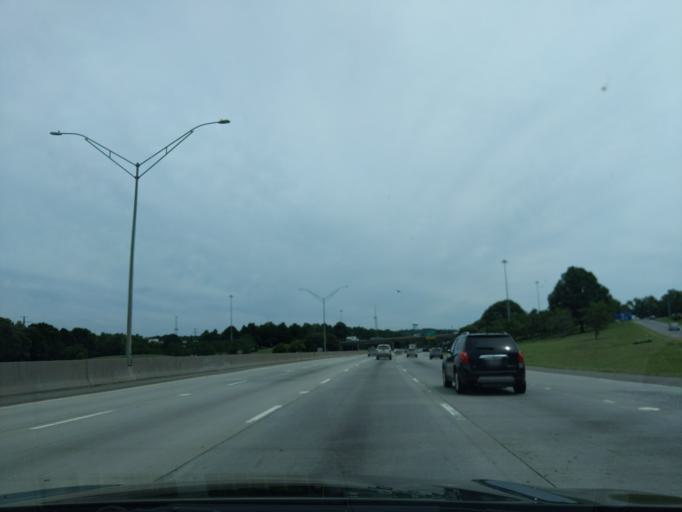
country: US
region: North Carolina
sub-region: Cabarrus County
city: Harrisburg
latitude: 35.3089
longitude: -80.7597
